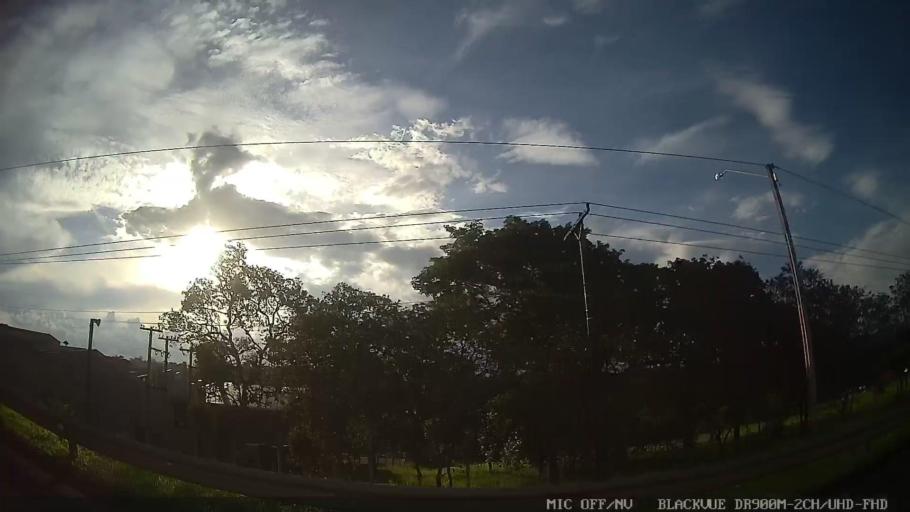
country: BR
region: Sao Paulo
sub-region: Tiete
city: Tiete
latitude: -23.0953
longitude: -47.7231
